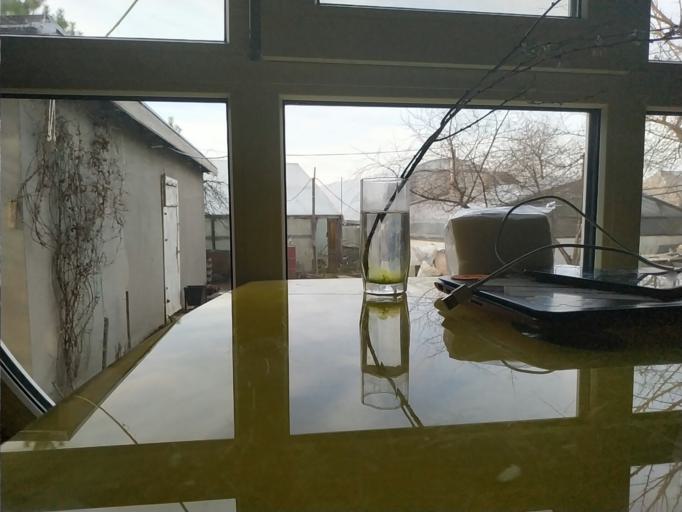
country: RU
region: Republic of Karelia
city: Suoyarvi
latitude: 61.8137
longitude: 32.2948
